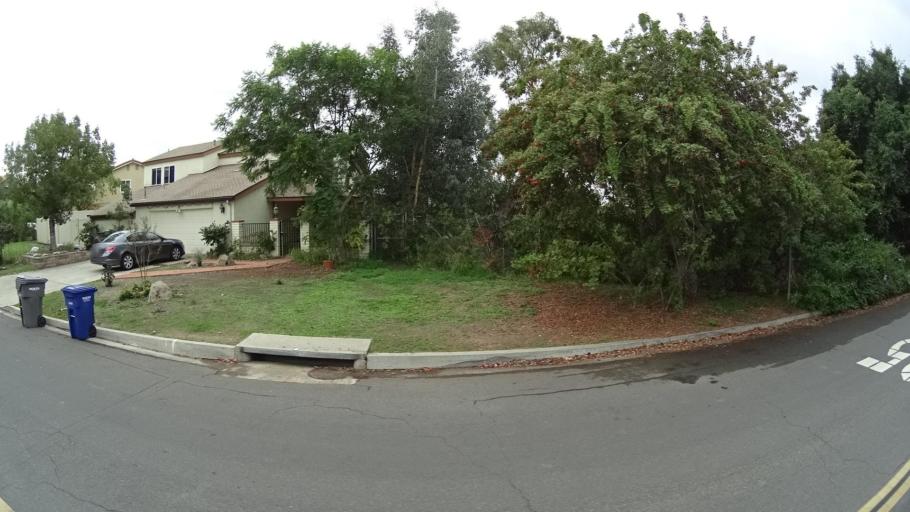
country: US
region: California
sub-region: San Diego County
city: Spring Valley
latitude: 32.7614
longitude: -116.9924
